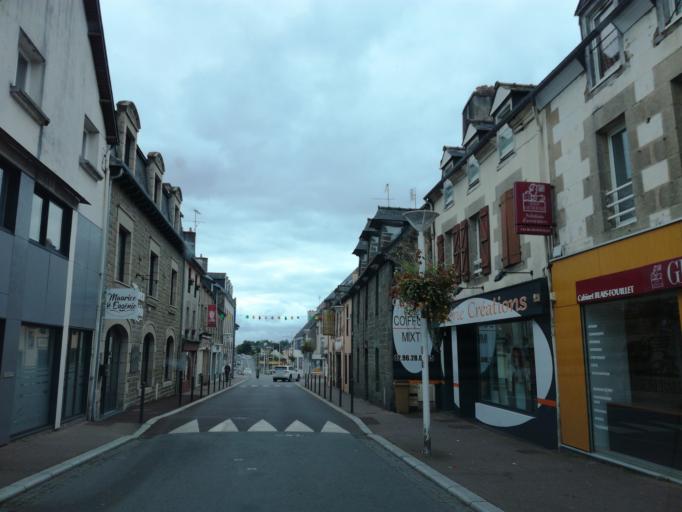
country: FR
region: Brittany
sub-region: Departement des Cotes-d'Armor
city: Loudeac
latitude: 48.1754
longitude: -2.7542
